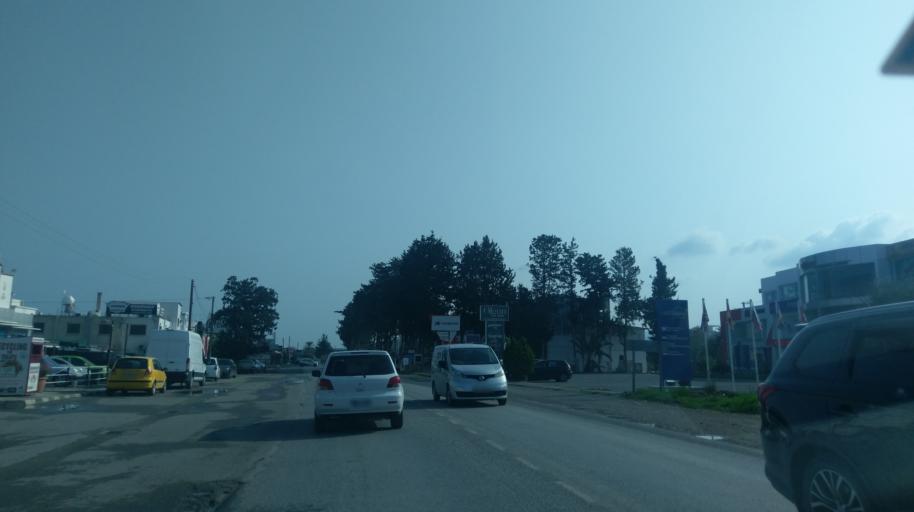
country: CY
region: Keryneia
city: Kyrenia
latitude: 35.3295
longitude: 33.3533
